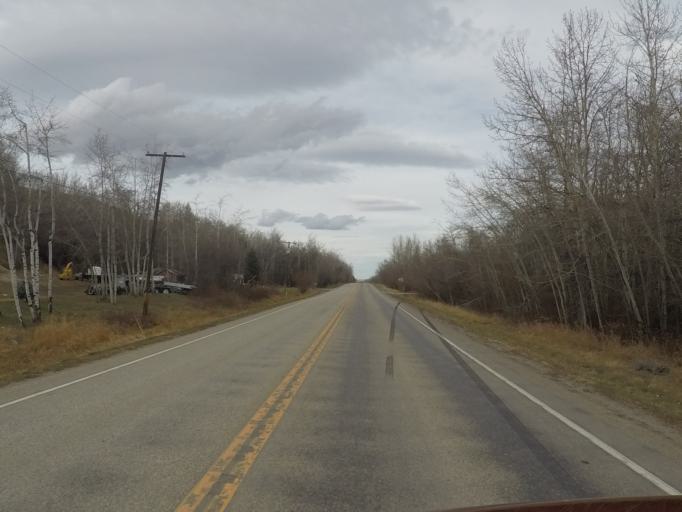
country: US
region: Montana
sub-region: Carbon County
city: Red Lodge
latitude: 45.2222
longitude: -109.2405
